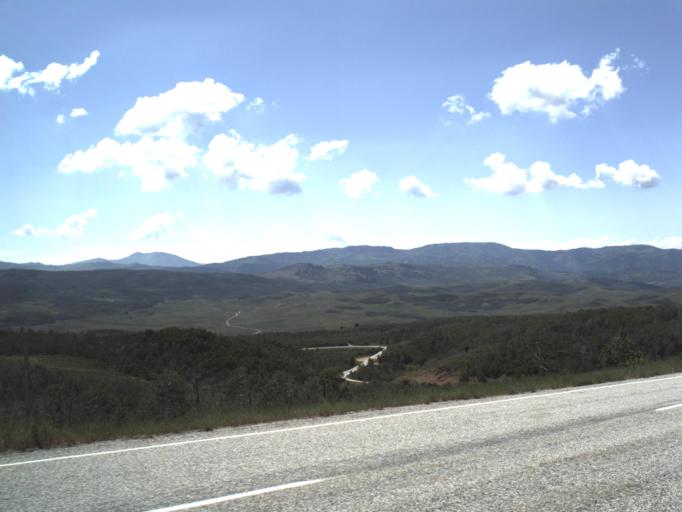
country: US
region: Utah
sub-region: Weber County
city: Wolf Creek
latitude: 41.4154
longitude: -111.5589
